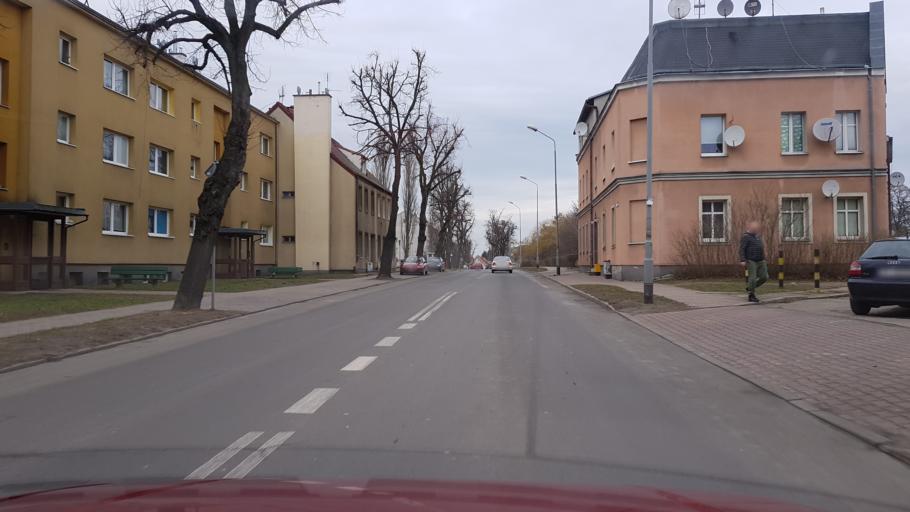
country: PL
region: West Pomeranian Voivodeship
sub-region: Powiat policki
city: Police
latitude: 53.5489
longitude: 14.5725
